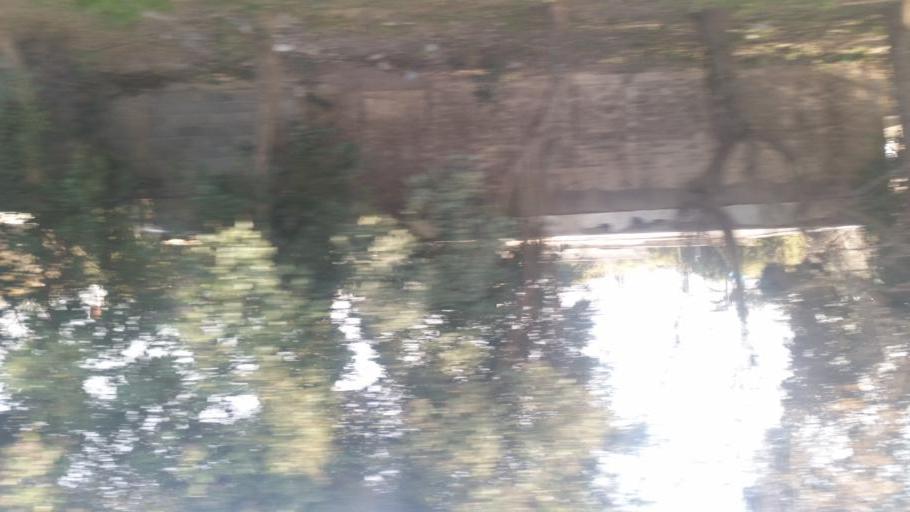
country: AR
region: Cordoba
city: Toledo
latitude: -31.5527
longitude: -64.0130
